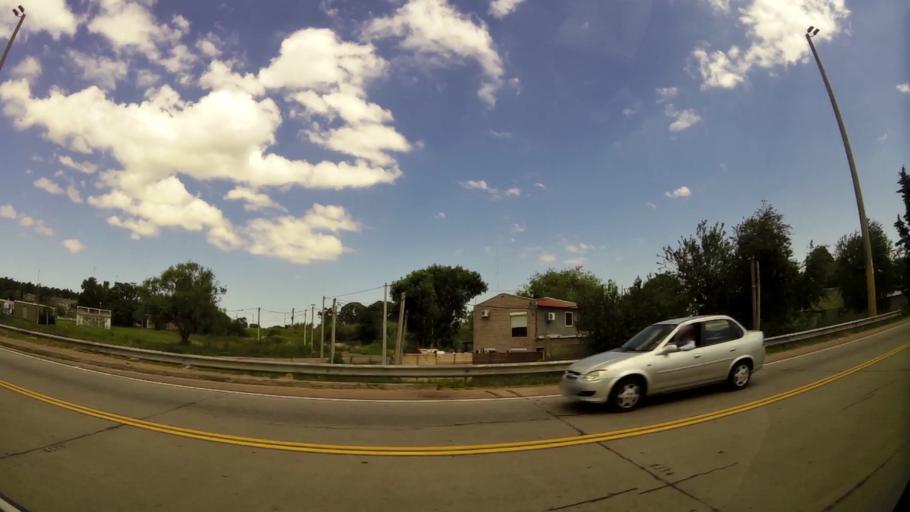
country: UY
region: Canelones
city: La Paz
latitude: -34.8243
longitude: -56.2455
